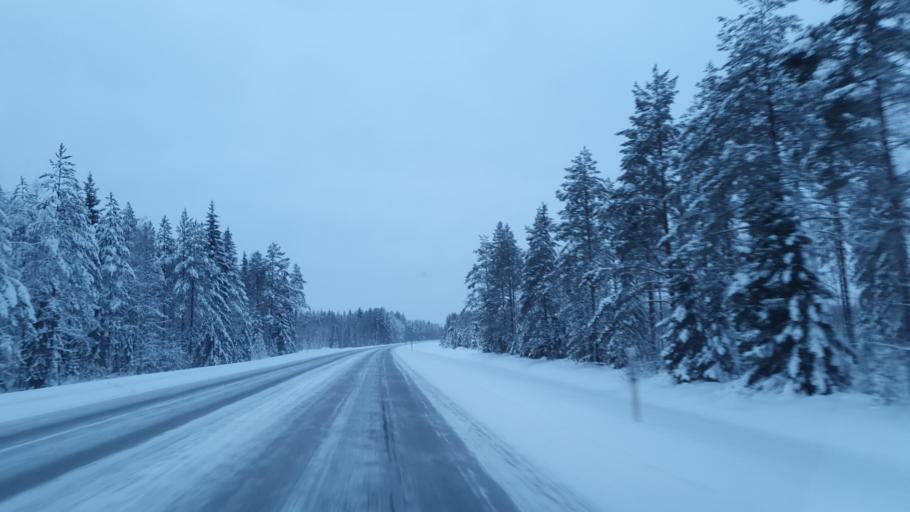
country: FI
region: Kainuu
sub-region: Kajaani
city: Vaala
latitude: 64.5981
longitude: 26.6902
